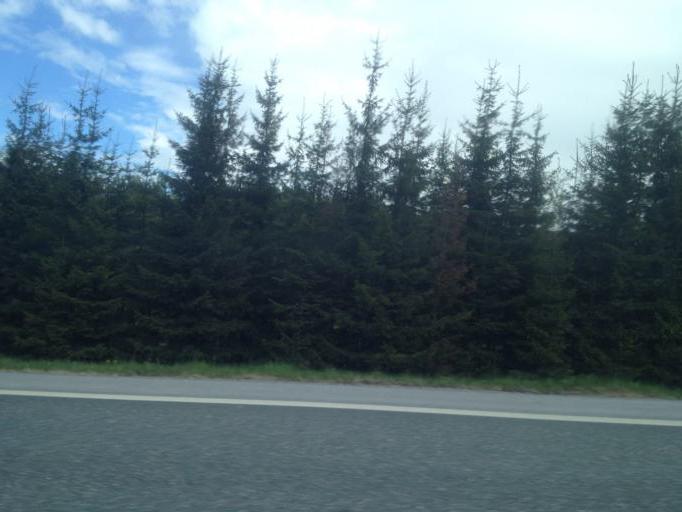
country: FI
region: Uusimaa
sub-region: Helsinki
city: Hyvinge
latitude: 60.6570
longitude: 24.7975
